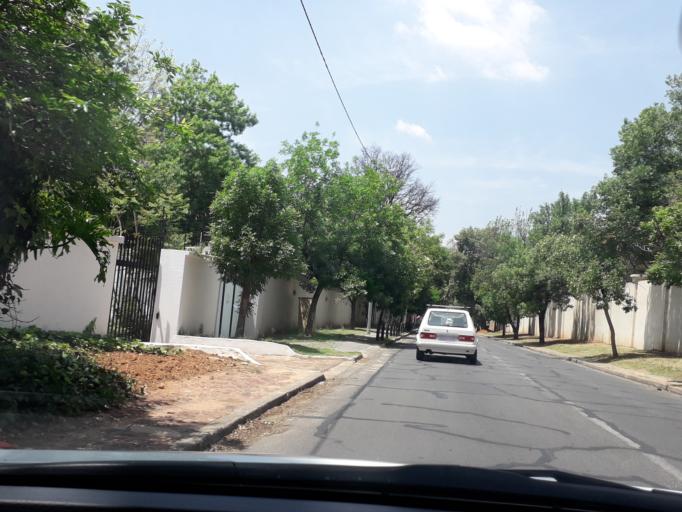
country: ZA
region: Gauteng
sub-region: City of Johannesburg Metropolitan Municipality
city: Johannesburg
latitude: -26.1052
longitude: 28.0291
